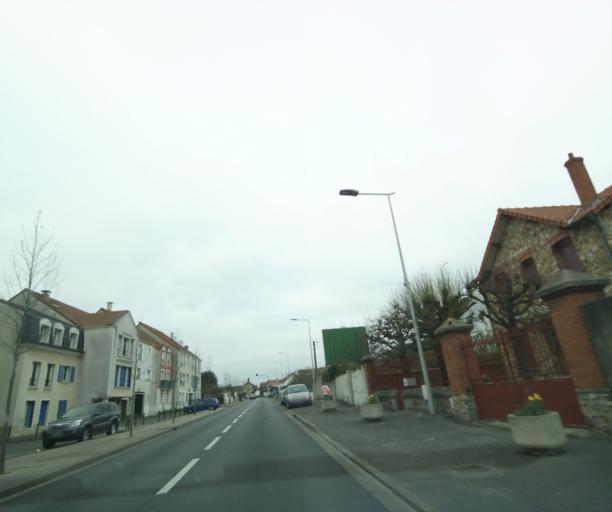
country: FR
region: Ile-de-France
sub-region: Departement des Yvelines
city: Carrieres-sous-Poissy
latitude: 48.9484
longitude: 2.0379
